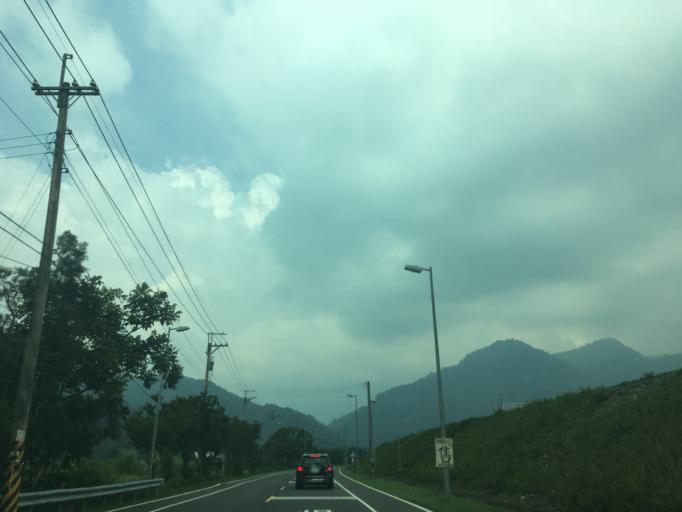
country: TW
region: Taiwan
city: Fengyuan
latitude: 24.2962
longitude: 120.8899
